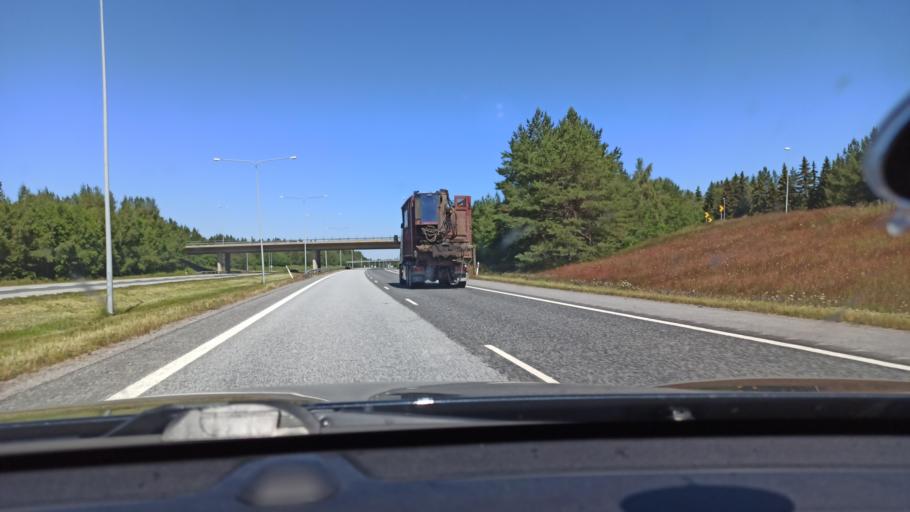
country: FI
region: Ostrobothnia
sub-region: Vaasa
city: Ristinummi
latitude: 63.0528
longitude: 21.7154
